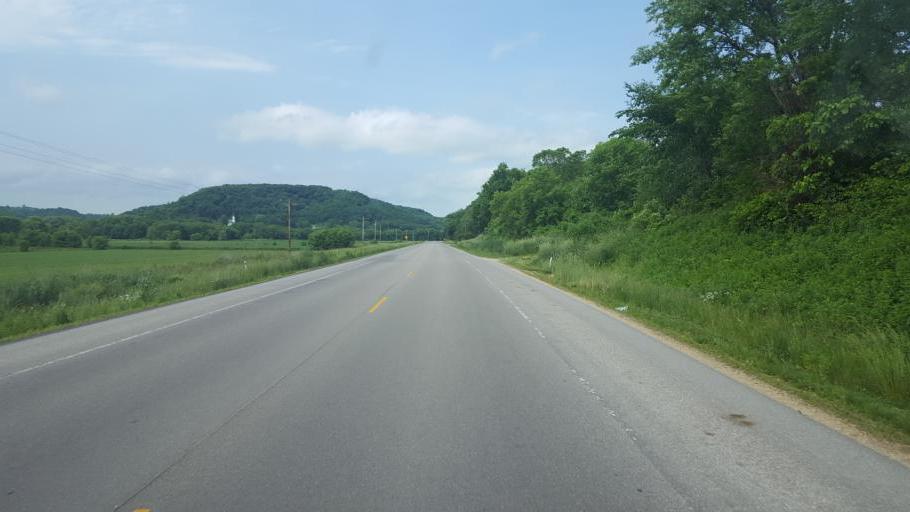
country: US
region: Wisconsin
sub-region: Monroe County
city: Cashton
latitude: 43.7300
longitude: -90.6543
